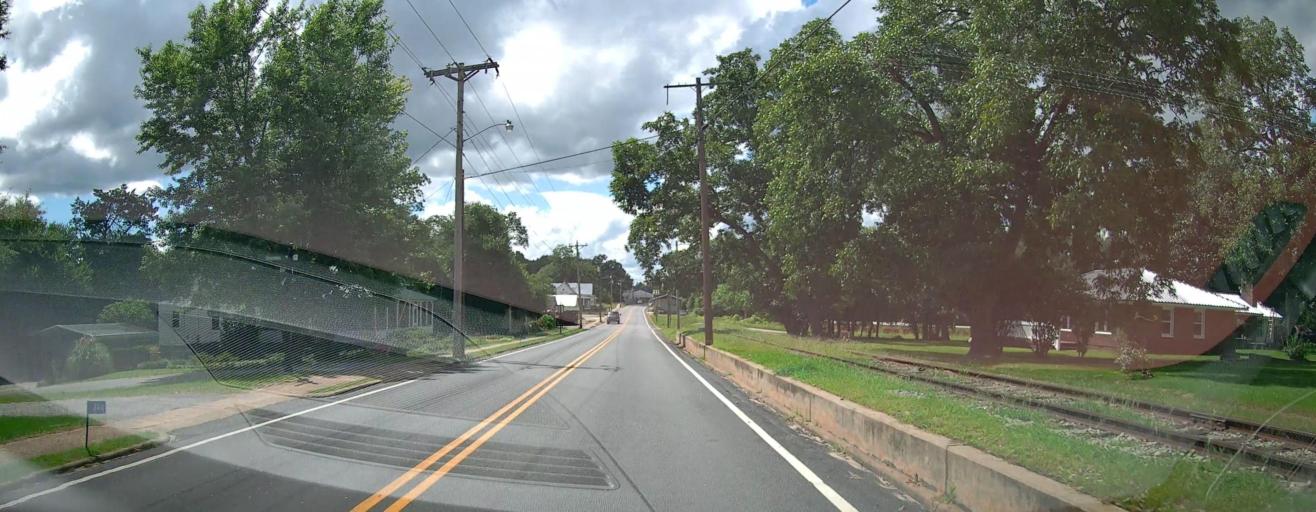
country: US
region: Georgia
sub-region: Chattahoochee County
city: Cusseta
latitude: 32.3064
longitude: -84.7779
